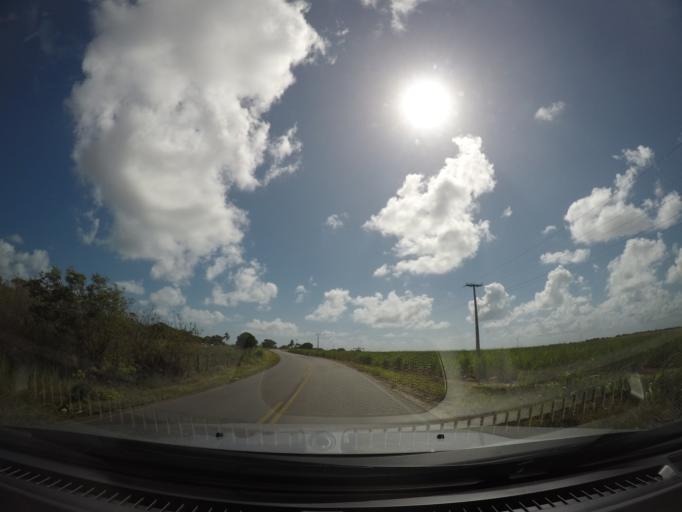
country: BR
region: Paraiba
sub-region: Pitimbu
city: Pitimbu
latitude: -7.4721
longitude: -34.8252
